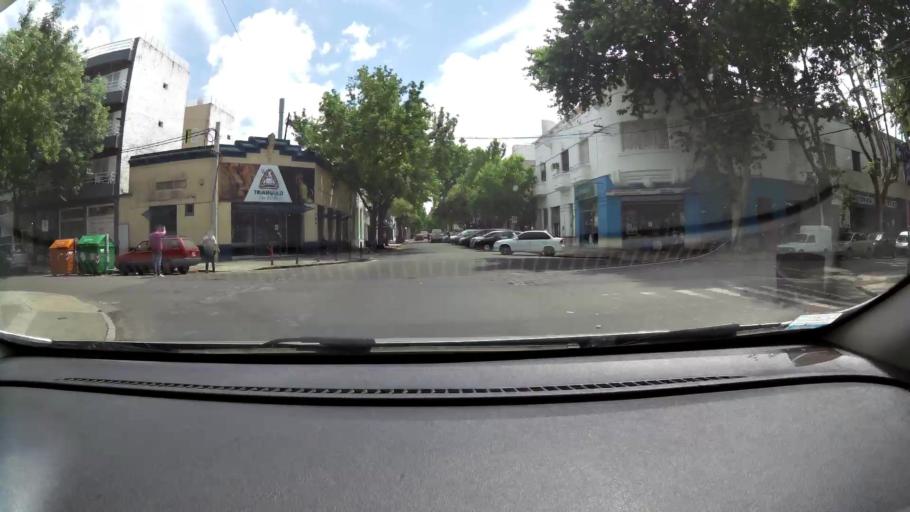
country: AR
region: Santa Fe
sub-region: Departamento de Rosario
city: Rosario
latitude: -32.9633
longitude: -60.6408
